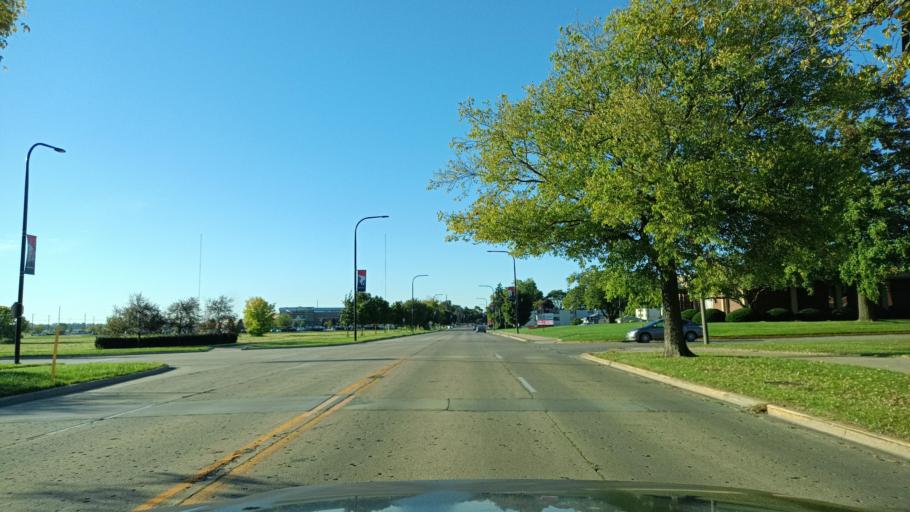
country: US
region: Illinois
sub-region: Champaign County
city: Champaign
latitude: 40.0877
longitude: -88.2382
